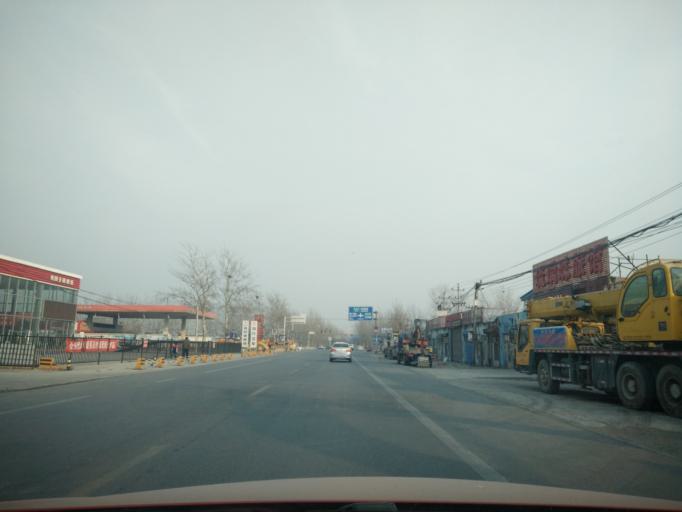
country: CN
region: Beijing
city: Yinghai
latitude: 39.7651
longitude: 116.4038
